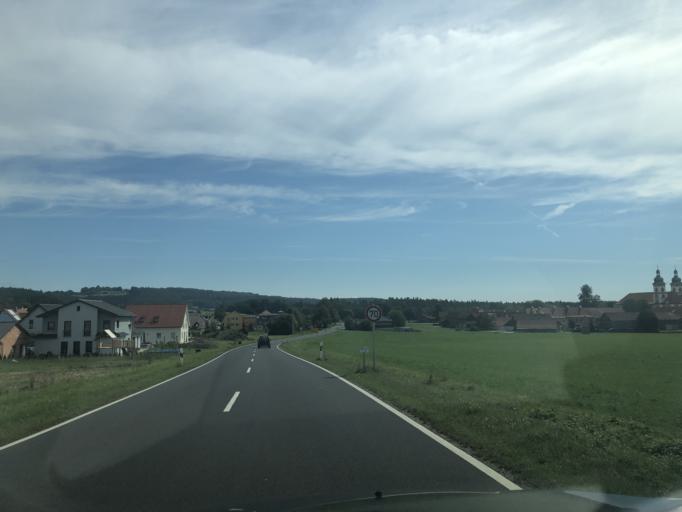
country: DE
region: Bavaria
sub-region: Upper Palatinate
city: Speinshart
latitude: 49.7892
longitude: 11.8153
